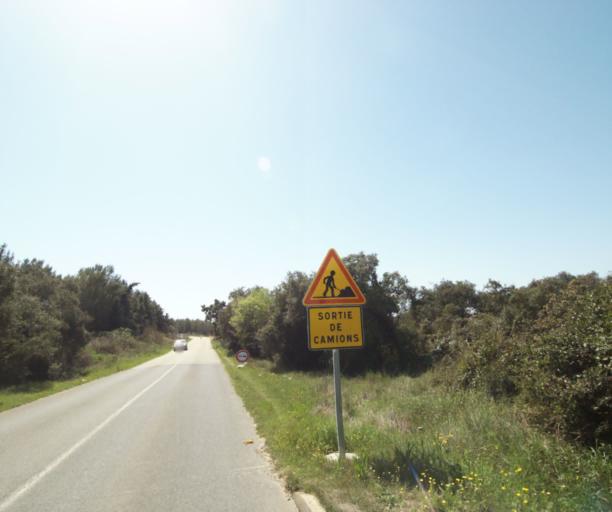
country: FR
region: Languedoc-Roussillon
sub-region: Departement de l'Herault
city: Castries
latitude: 43.6697
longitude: 3.9915
